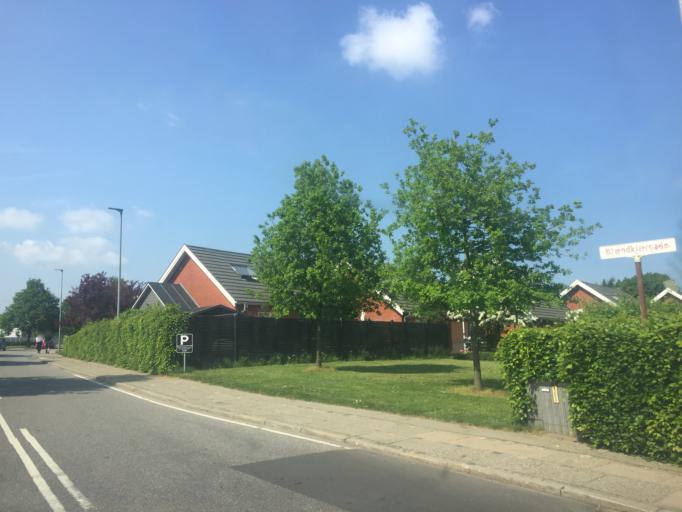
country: DK
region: South Denmark
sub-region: Kolding Kommune
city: Kolding
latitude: 55.4770
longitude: 9.4848
